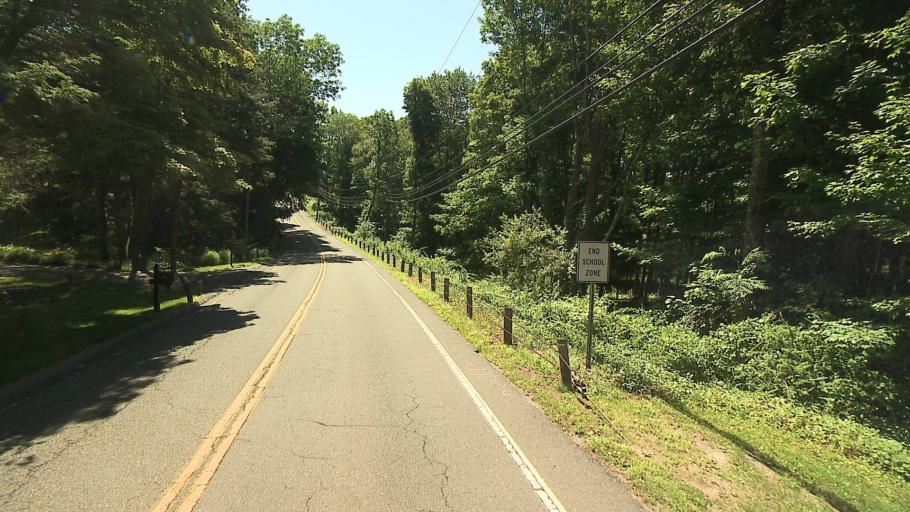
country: US
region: Connecticut
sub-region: Fairfield County
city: Ridgefield
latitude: 41.2963
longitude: -73.5335
